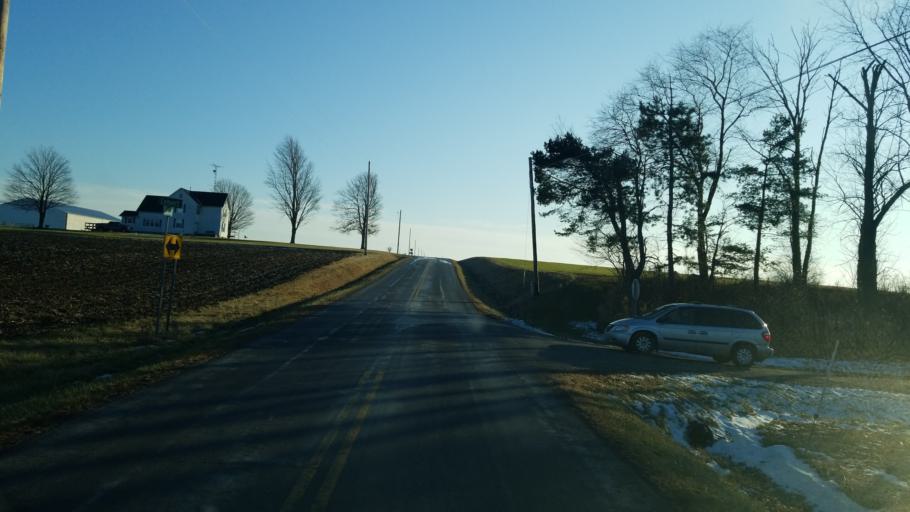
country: US
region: Ohio
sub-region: Crawford County
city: Bucyrus
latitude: 40.8897
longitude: -82.9017
